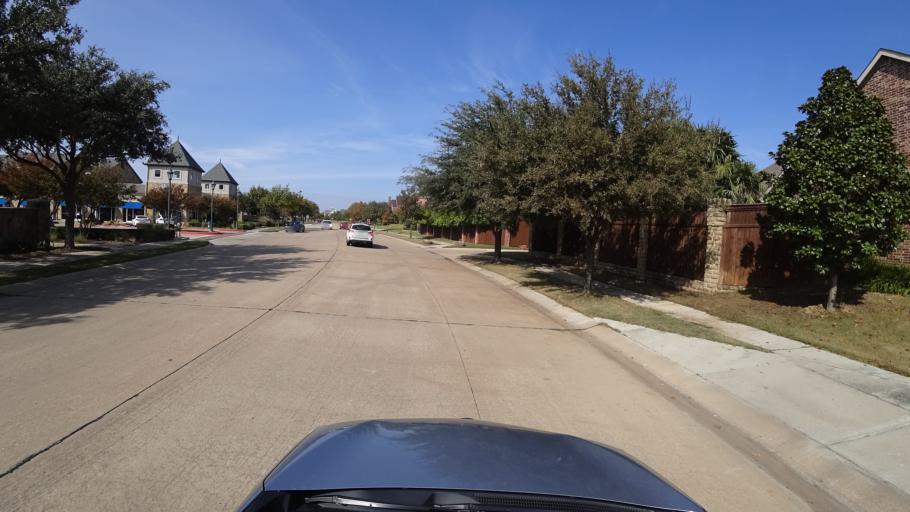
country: US
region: Texas
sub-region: Denton County
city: The Colony
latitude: 33.0357
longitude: -96.8968
